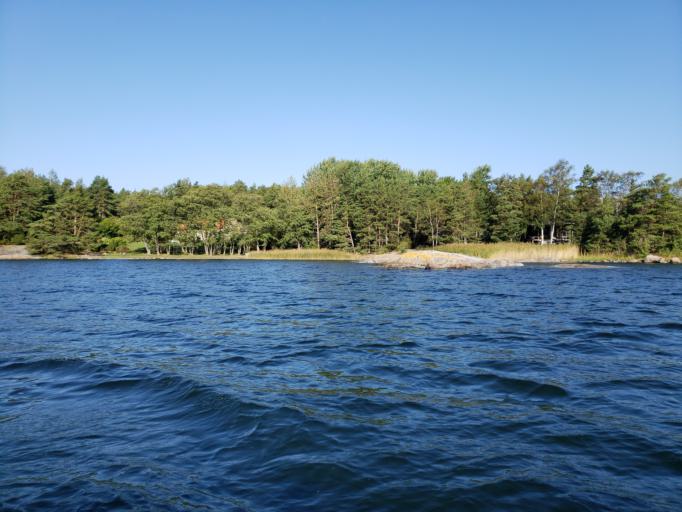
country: FI
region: Varsinais-Suomi
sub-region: Aboland-Turunmaa
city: Dragsfjaerd
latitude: 59.9103
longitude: 22.3768
